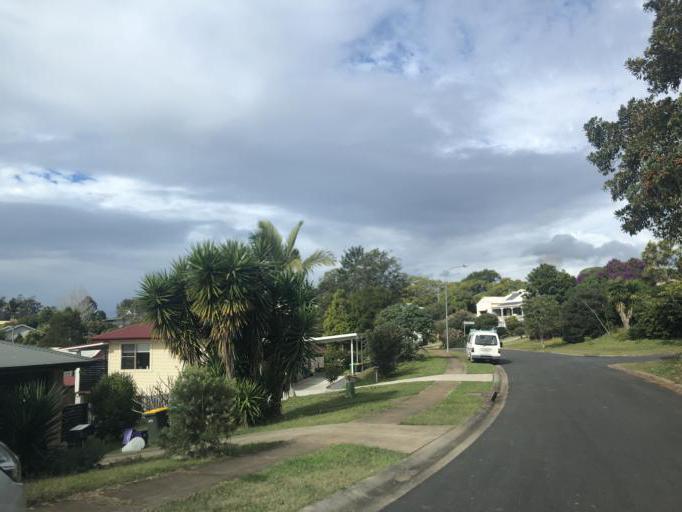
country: AU
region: New South Wales
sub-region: Bellingen
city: Bellingen
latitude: -30.4447
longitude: 152.9013
